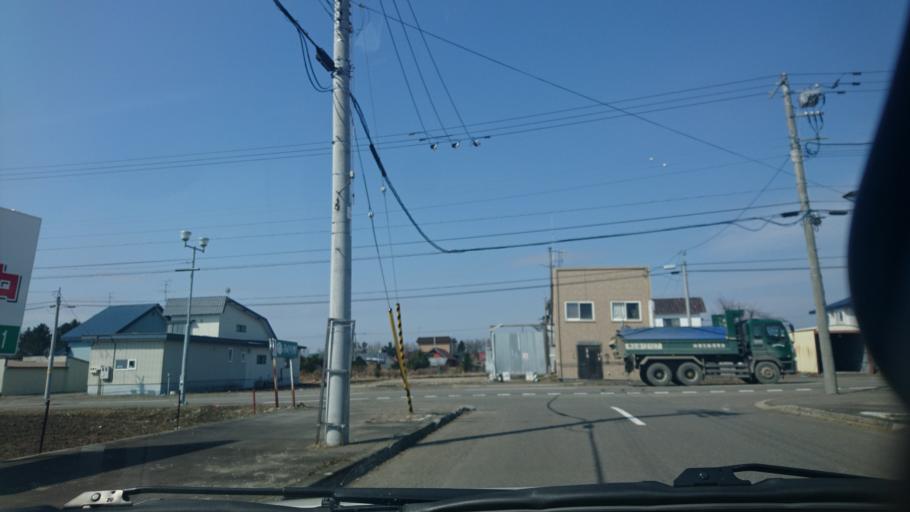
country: JP
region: Hokkaido
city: Otofuke
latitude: 43.0937
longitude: 143.2294
